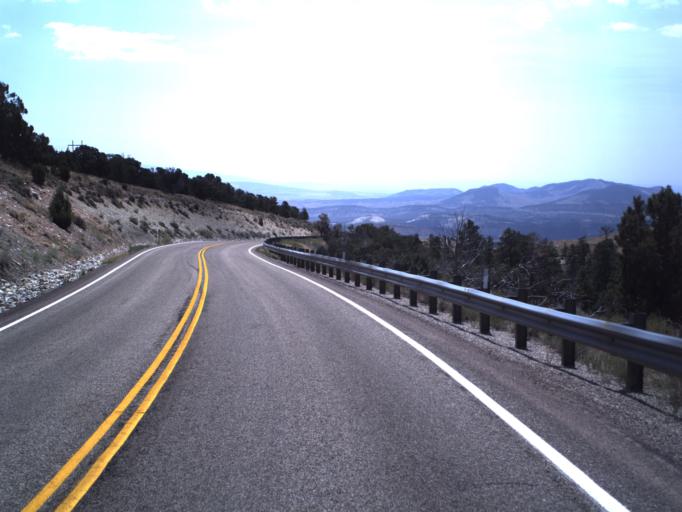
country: US
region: Utah
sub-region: Uintah County
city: Vernal
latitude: 40.6424
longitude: -109.4838
